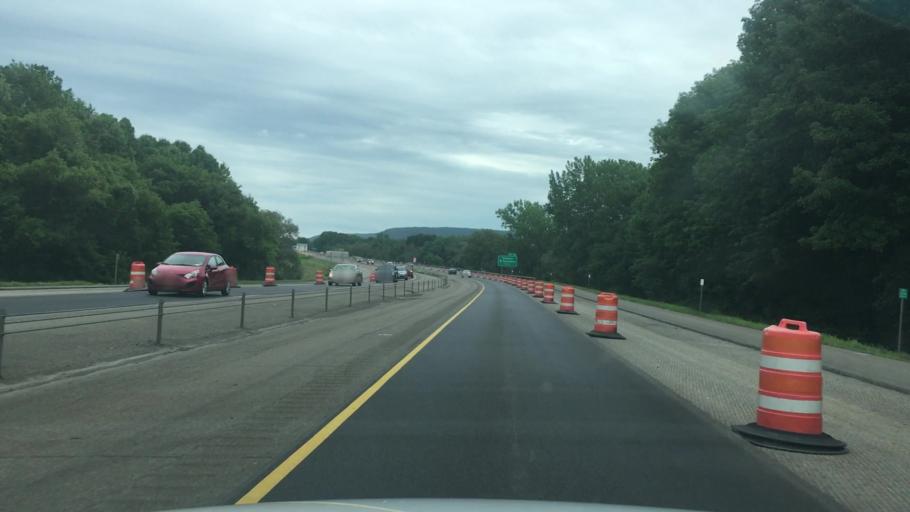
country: US
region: New York
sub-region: Otsego County
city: Oneonta
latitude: 42.4527
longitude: -75.0356
